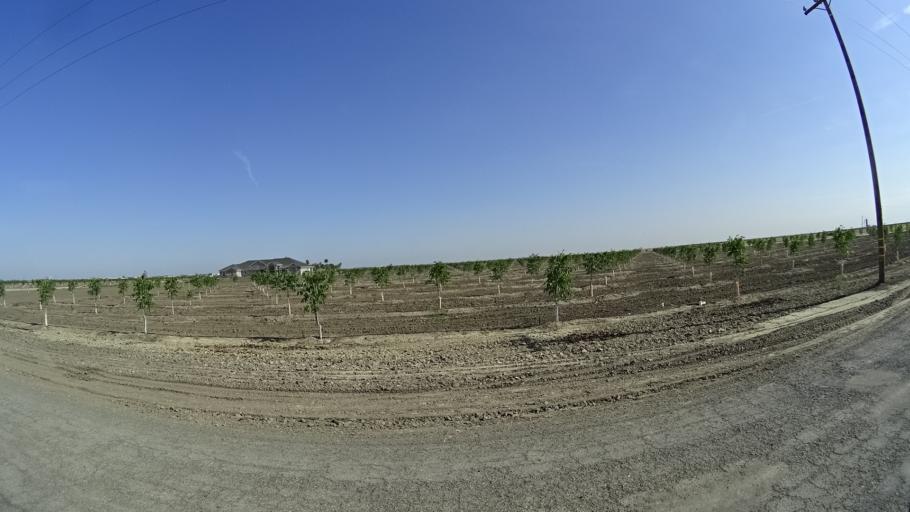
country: US
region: California
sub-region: Kings County
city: Home Garden
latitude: 36.2261
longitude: -119.5398
